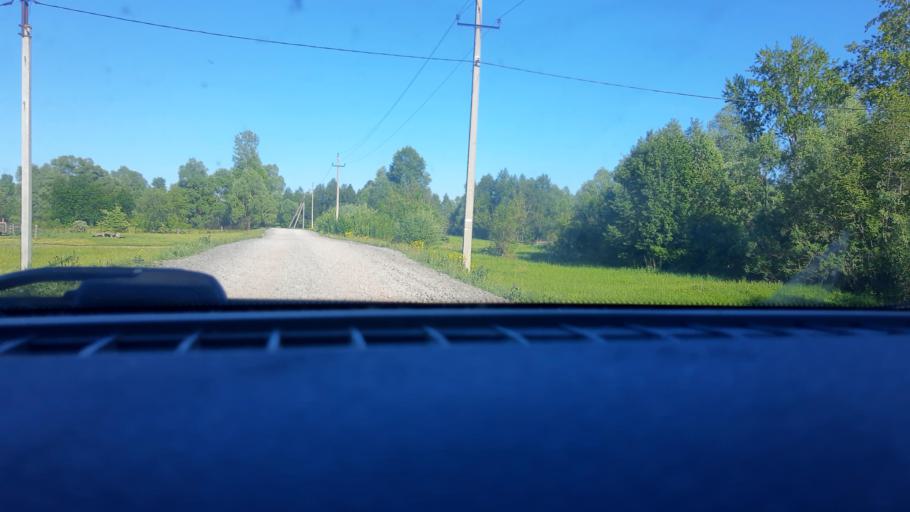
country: RU
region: Bashkortostan
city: Ulukulevo
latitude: 54.5598
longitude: 56.3300
